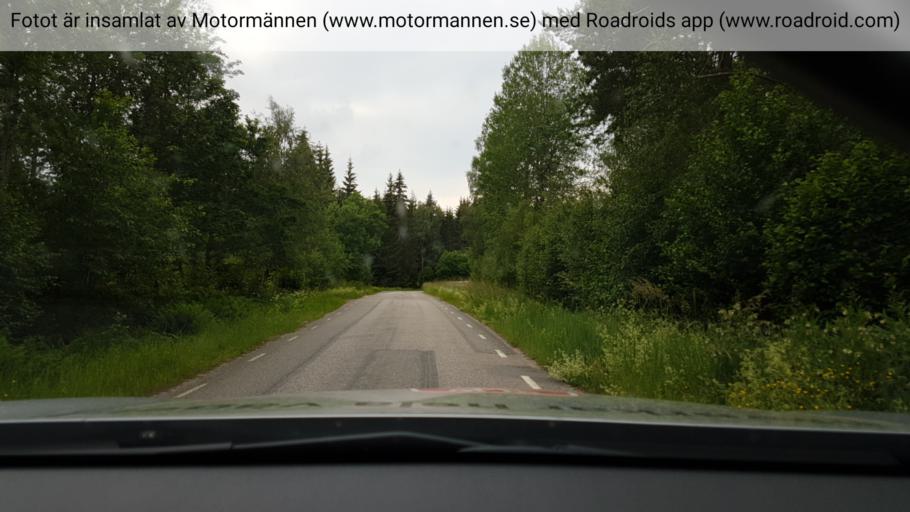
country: SE
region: Joenkoeping
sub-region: Mullsjo Kommun
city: Mullsjoe
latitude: 57.9395
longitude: 13.6661
